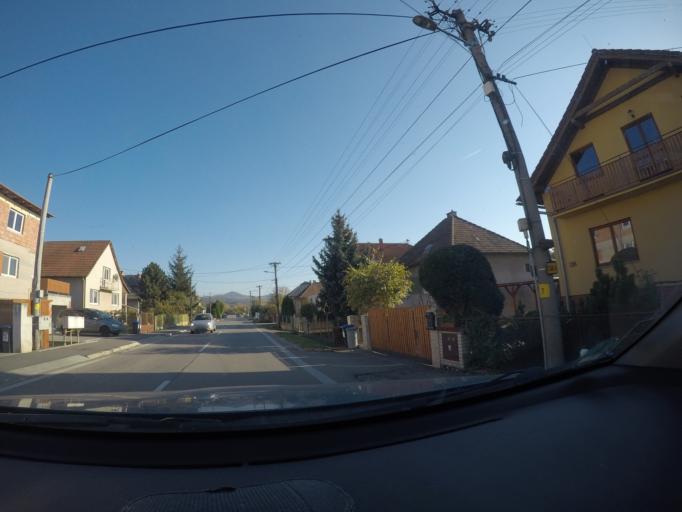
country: SK
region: Trenciansky
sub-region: Okres Trencin
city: Trencin
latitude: 48.9088
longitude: 18.0551
